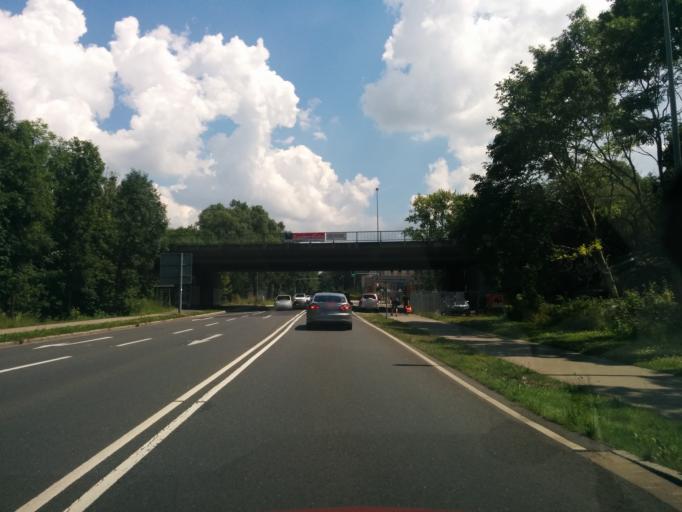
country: DE
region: Lower Saxony
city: Goettingen
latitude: 51.5561
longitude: 9.9413
